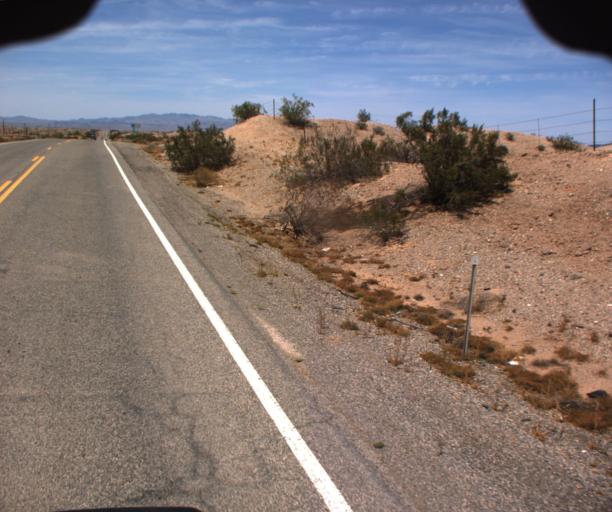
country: US
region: Arizona
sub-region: La Paz County
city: Parker
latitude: 34.0145
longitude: -114.2457
